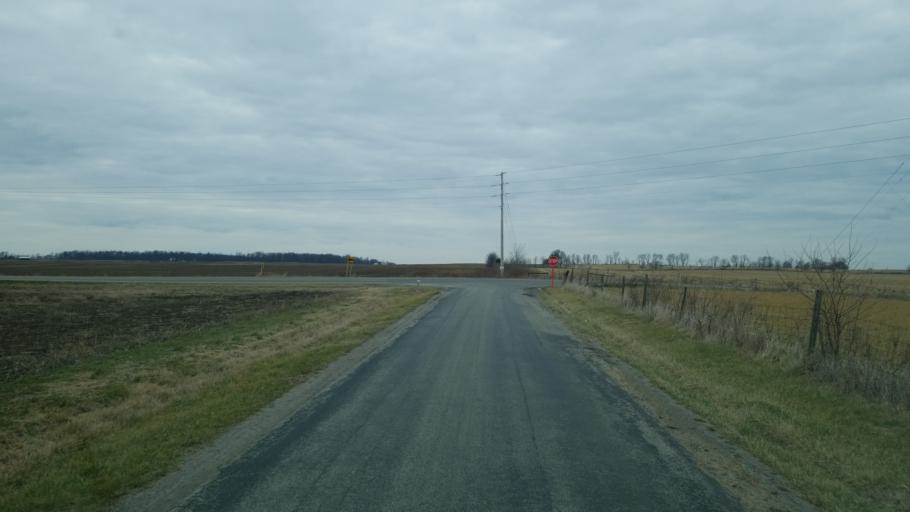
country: US
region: Ohio
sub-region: Highland County
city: Leesburg
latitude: 39.2623
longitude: -83.5292
